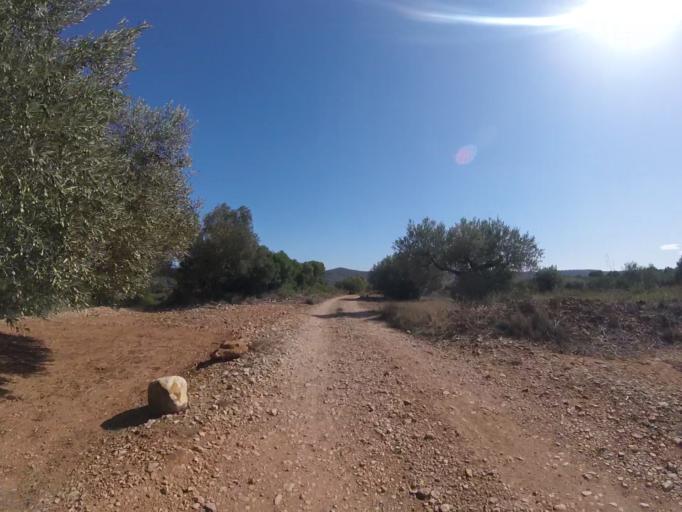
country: ES
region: Valencia
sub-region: Provincia de Castello
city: Cuevas de Vinroma
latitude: 40.2802
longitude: 0.0859
